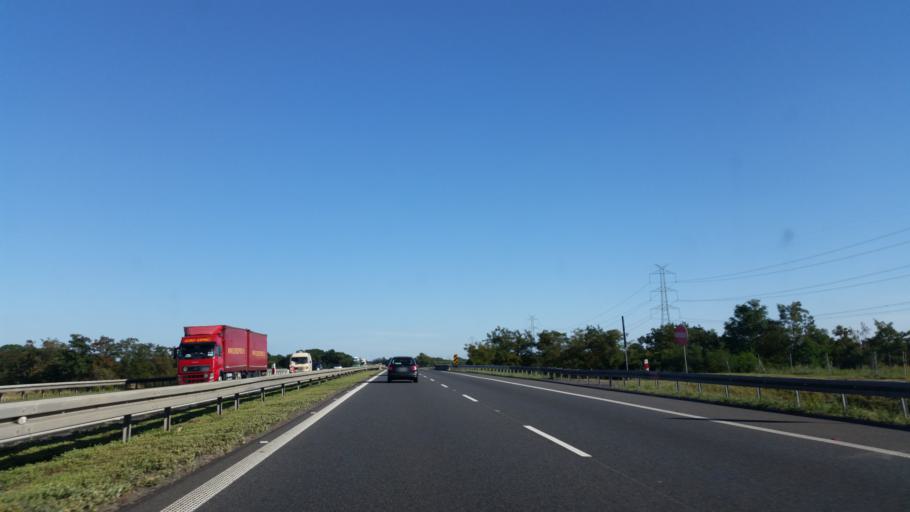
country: PL
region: Lower Silesian Voivodeship
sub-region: Powiat strzelinski
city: Wiazow
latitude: 50.8271
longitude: 17.2941
